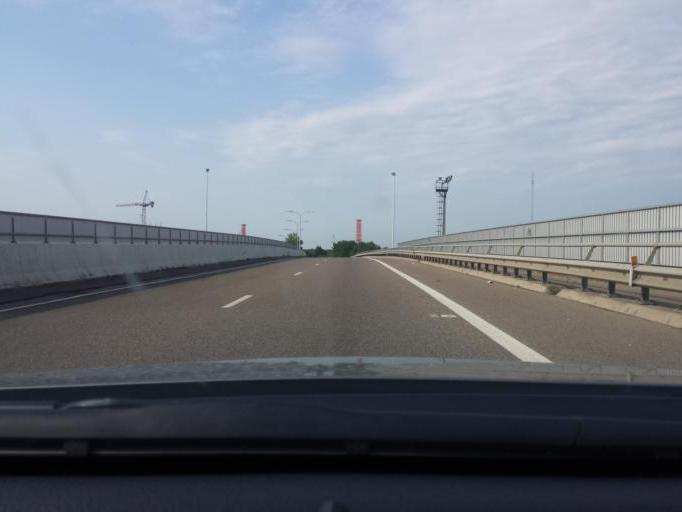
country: BE
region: Flanders
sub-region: Provincie Limburg
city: Hasselt
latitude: 50.9341
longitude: 5.3149
